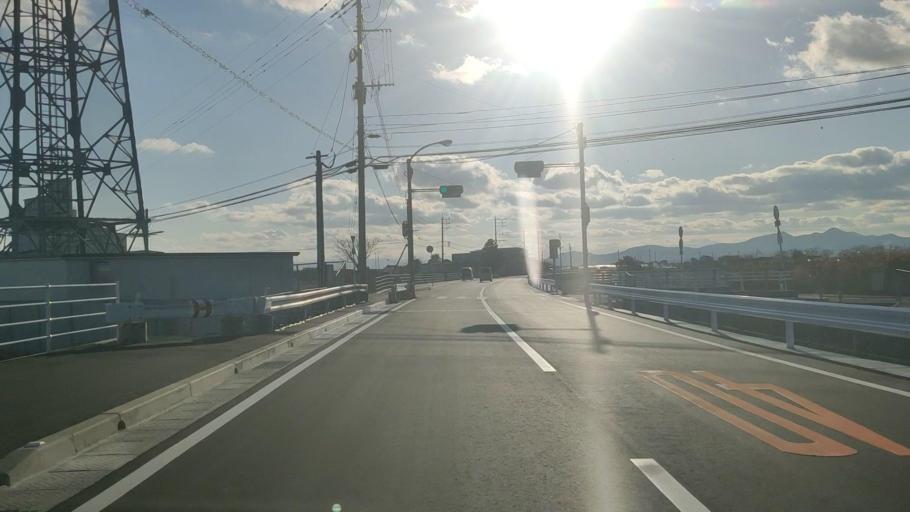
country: JP
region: Saga Prefecture
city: Saga-shi
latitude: 33.3035
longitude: 130.2546
